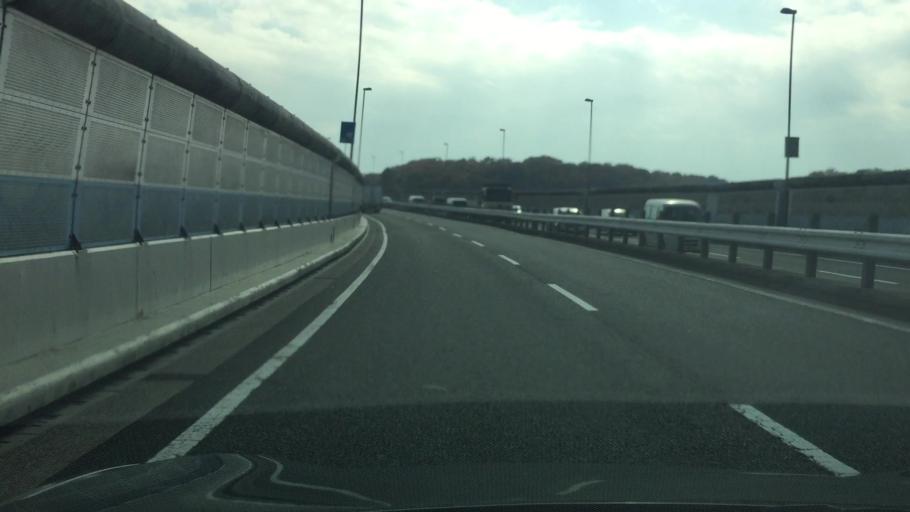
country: JP
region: Saitama
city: Wako
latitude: 35.7883
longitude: 139.6437
